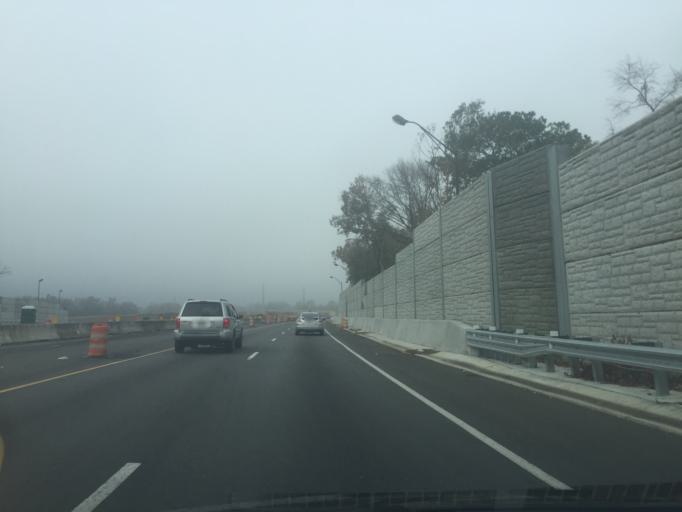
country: US
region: Georgia
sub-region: Chatham County
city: Georgetown
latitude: 31.9851
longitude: -81.2125
